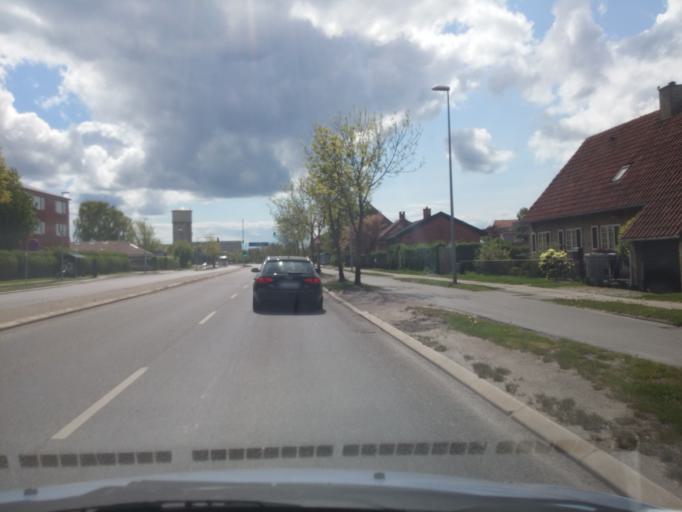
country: DK
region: Capital Region
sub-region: Tarnby Kommune
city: Tarnby
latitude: 55.6363
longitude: 12.6003
